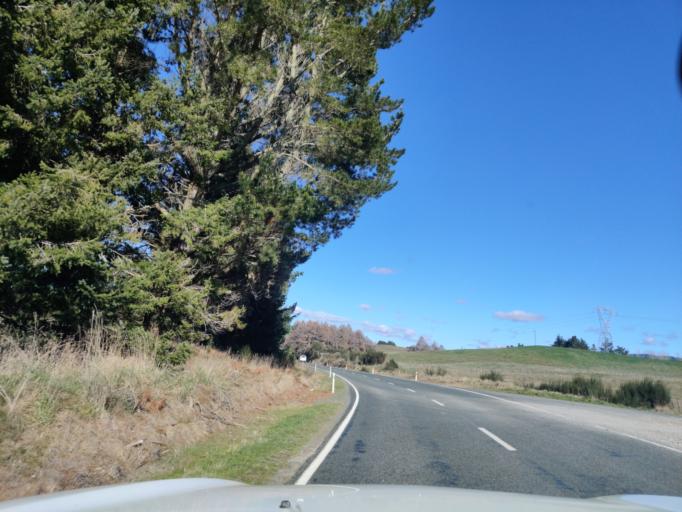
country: NZ
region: Waikato
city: Turangi
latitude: -38.8401
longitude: 175.6870
